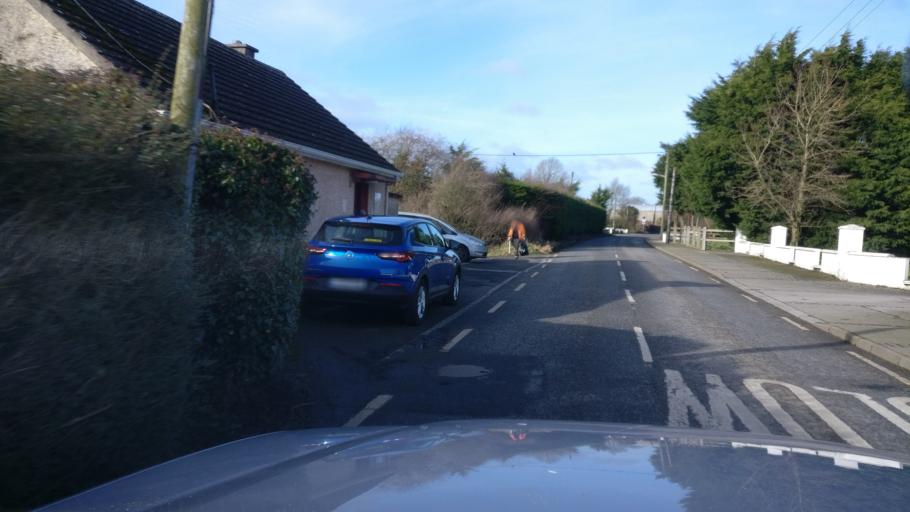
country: IE
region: Leinster
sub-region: Kilkenny
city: Castlecomer
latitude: 52.8616
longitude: -7.1637
